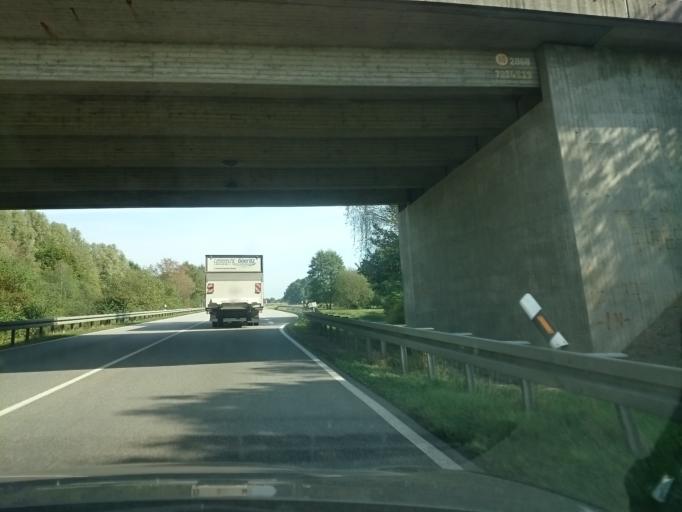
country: DE
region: Bavaria
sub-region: Upper Bavaria
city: Reichertshofen
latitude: 48.6371
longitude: 11.4562
